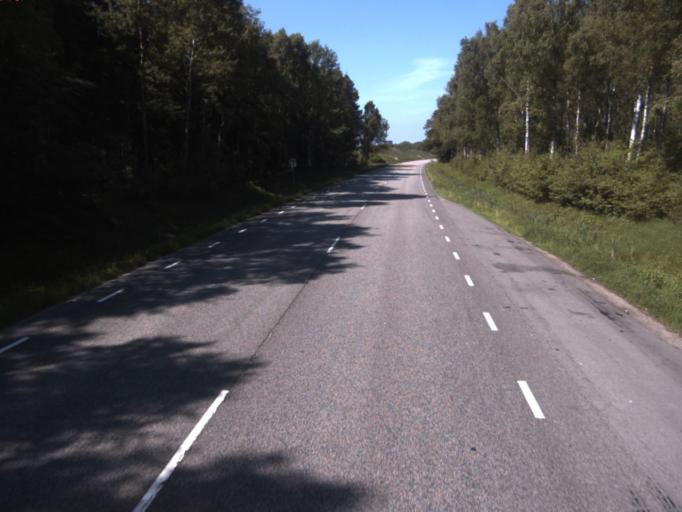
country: SE
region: Skane
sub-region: Helsingborg
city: Odakra
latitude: 56.0540
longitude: 12.7726
